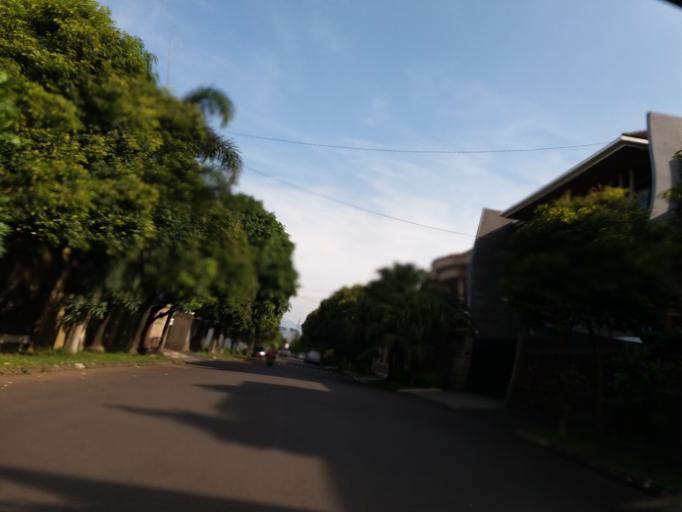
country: ID
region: West Java
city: Bandung
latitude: -6.9602
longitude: 107.6302
